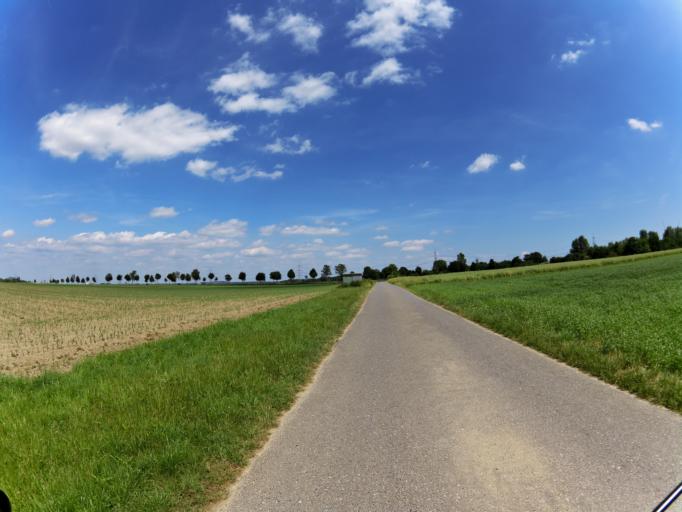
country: DE
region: North Rhine-Westphalia
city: Geilenkirchen
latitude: 51.0156
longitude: 6.1117
